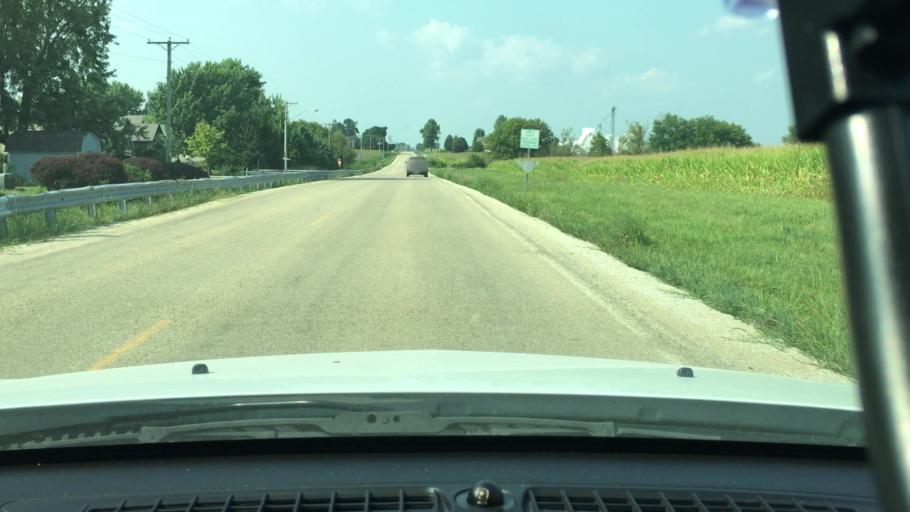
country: US
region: Illinois
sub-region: DeKalb County
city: Waterman
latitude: 41.7764
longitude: -88.7738
